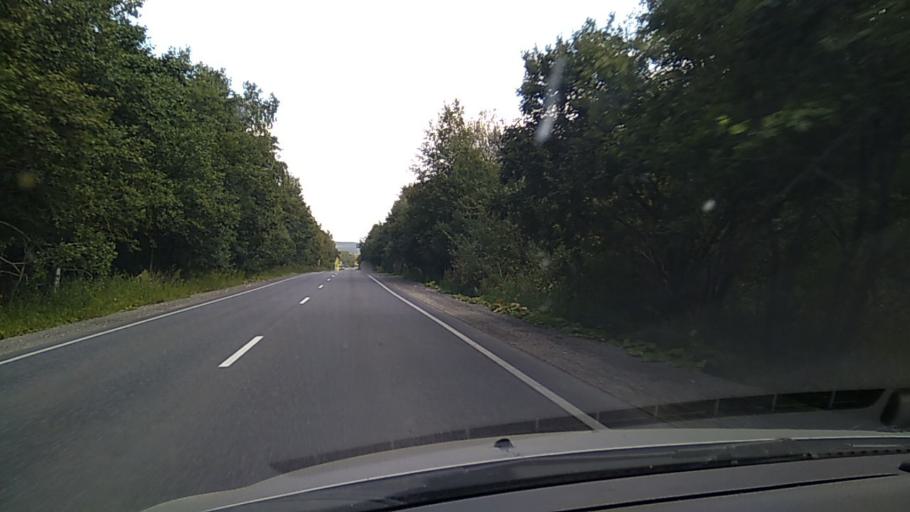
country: RU
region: Chelyabinsk
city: Syrostan
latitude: 55.1211
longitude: 59.8115
